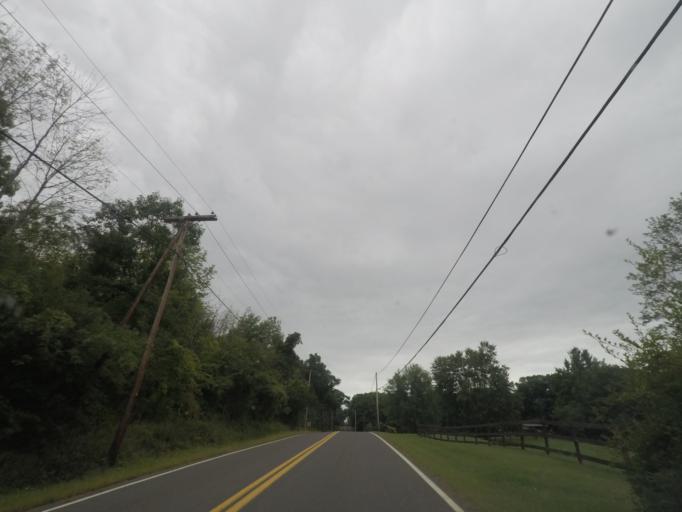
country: US
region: New York
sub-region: Rensselaer County
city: Nassau
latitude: 42.4516
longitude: -73.5718
